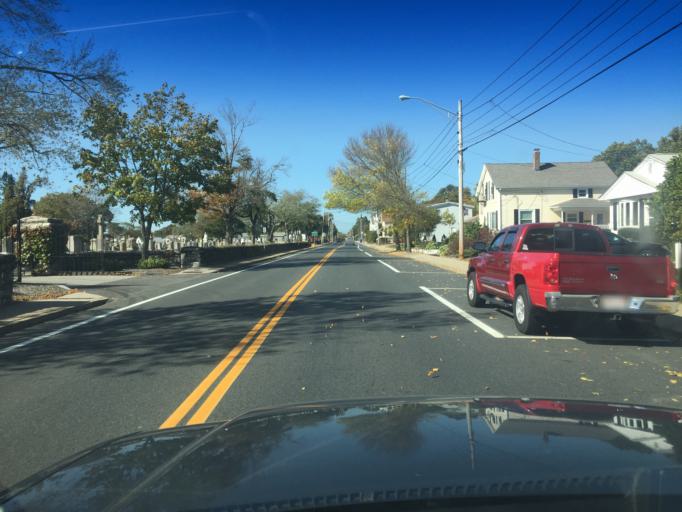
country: US
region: Rhode Island
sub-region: Providence County
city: Pawtucket
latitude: 41.8573
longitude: -71.3647
